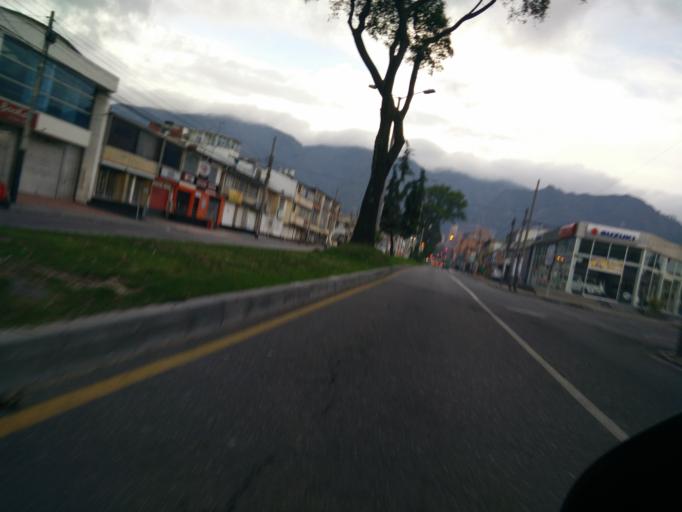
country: CO
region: Bogota D.C.
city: Barrio San Luis
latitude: 4.6619
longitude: -74.0655
